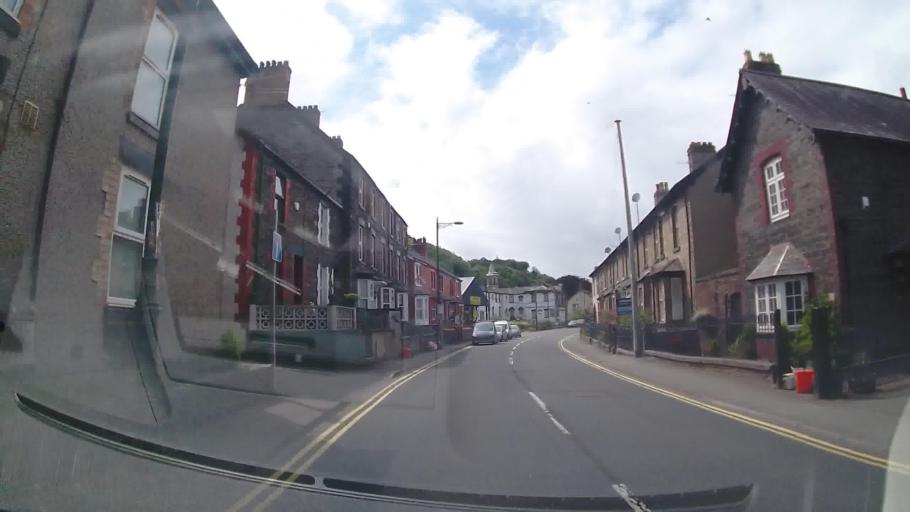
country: GB
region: Wales
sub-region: Denbighshire
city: Corwen
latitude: 52.9785
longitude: -3.3685
